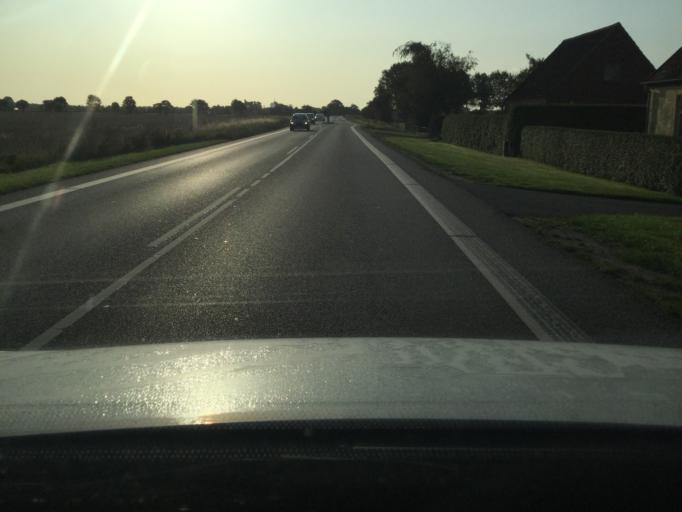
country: DK
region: Zealand
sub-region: Lolland Kommune
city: Nakskov
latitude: 54.8047
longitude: 11.2343
